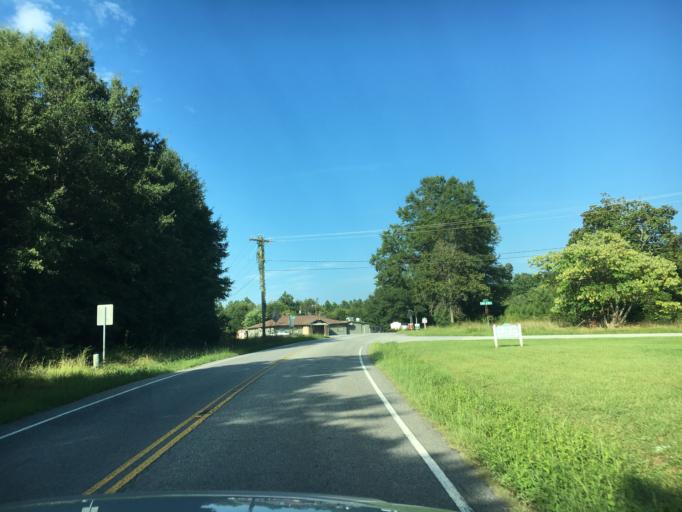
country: US
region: South Carolina
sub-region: Spartanburg County
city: Boiling Springs
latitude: 35.0583
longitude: -81.9475
